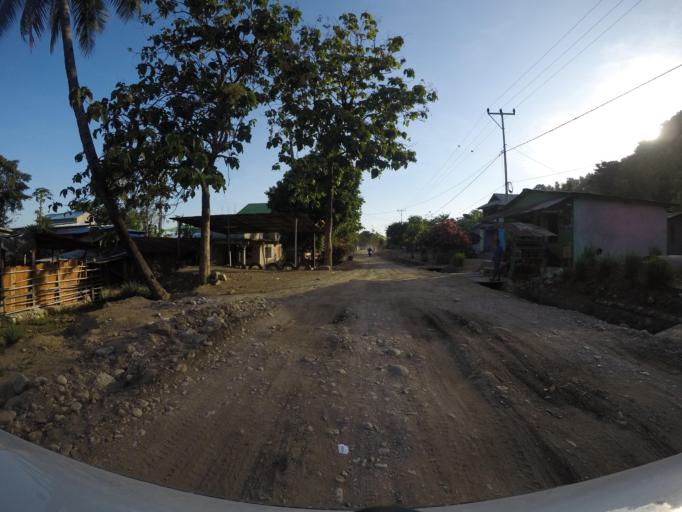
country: TL
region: Viqueque
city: Viqueque
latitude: -8.7996
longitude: 126.5533
